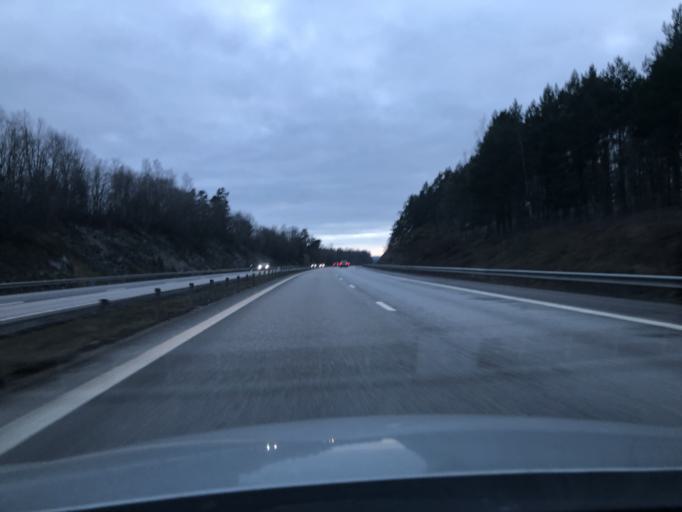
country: SE
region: Joenkoeping
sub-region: Jonkopings Kommun
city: Graenna
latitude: 58.0193
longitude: 14.4762
